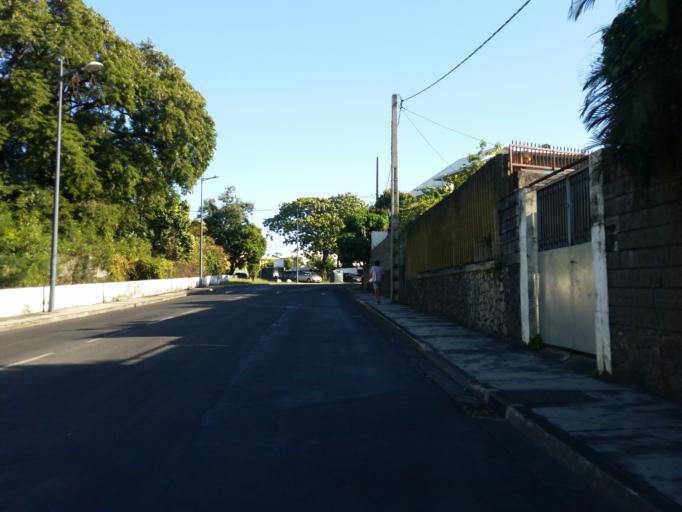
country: RE
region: Reunion
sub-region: Reunion
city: Saint-Denis
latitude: -20.8925
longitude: 55.4554
